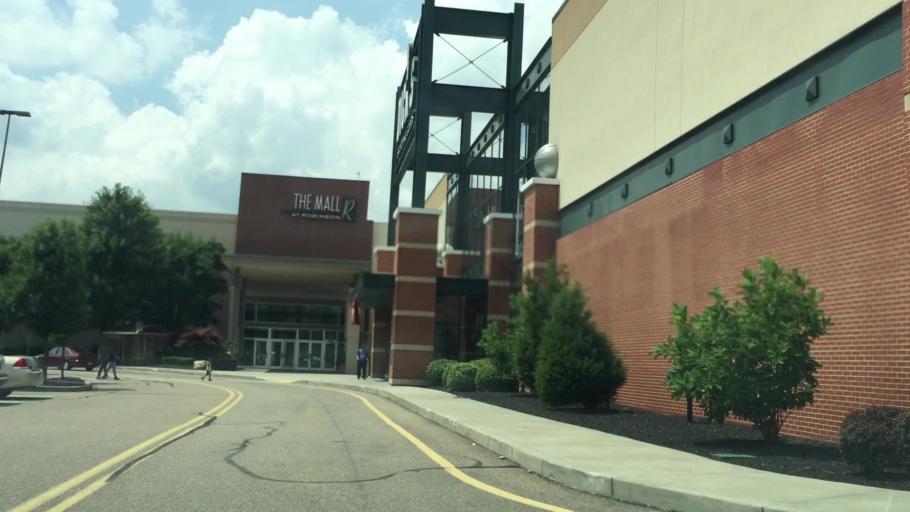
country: US
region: Pennsylvania
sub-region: Allegheny County
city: Rennerdale
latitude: 40.4527
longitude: -80.1563
